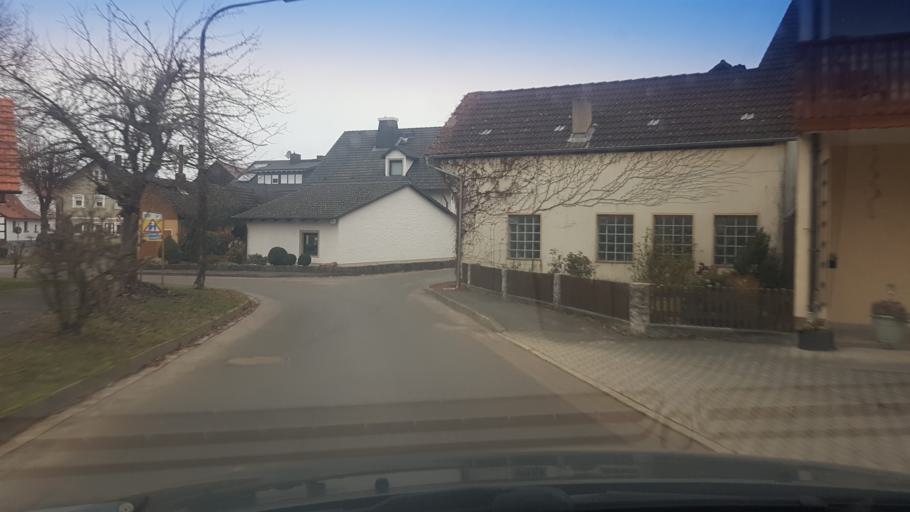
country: DE
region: Bavaria
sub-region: Upper Franconia
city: Weismain
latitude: 50.0319
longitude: 11.2680
